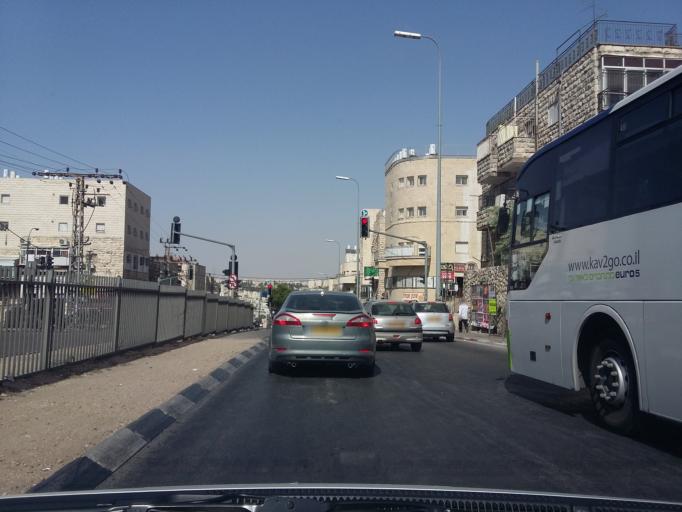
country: IL
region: Jerusalem
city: West Jerusalem
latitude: 31.7935
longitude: 35.2147
